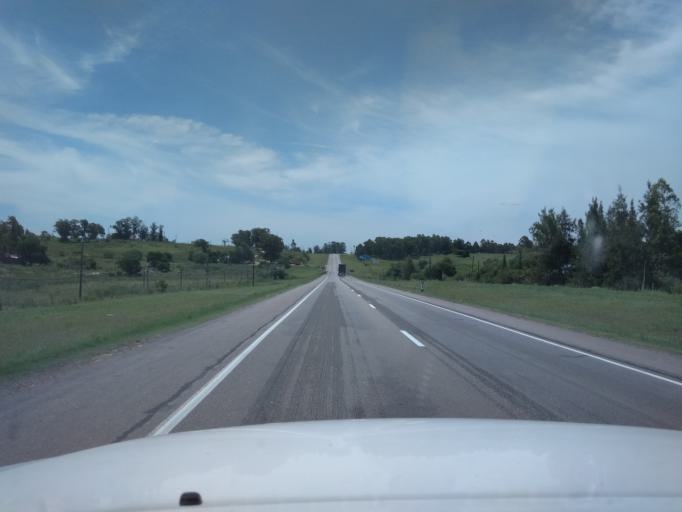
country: UY
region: Florida
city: Florida
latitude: -34.1278
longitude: -56.1870
